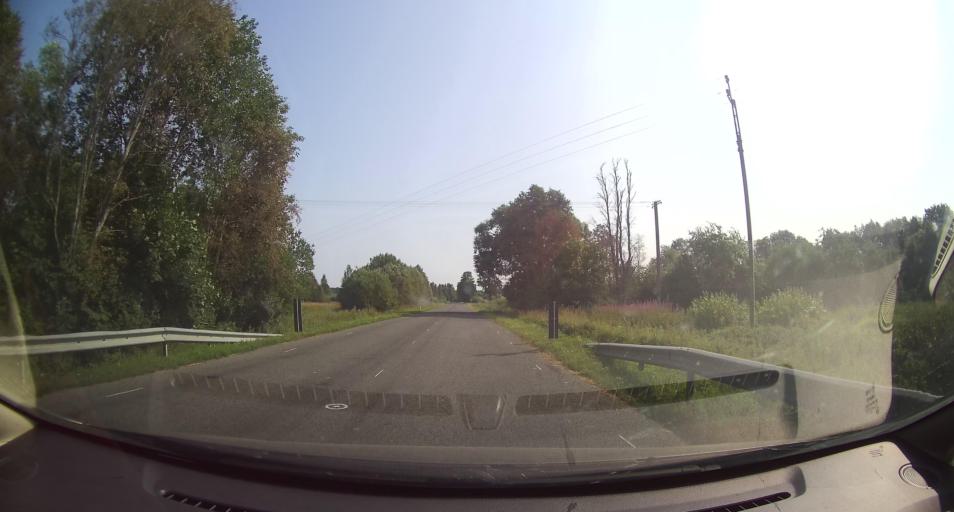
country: EE
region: Paernumaa
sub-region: Audru vald
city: Audru
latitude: 58.4991
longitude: 24.3396
